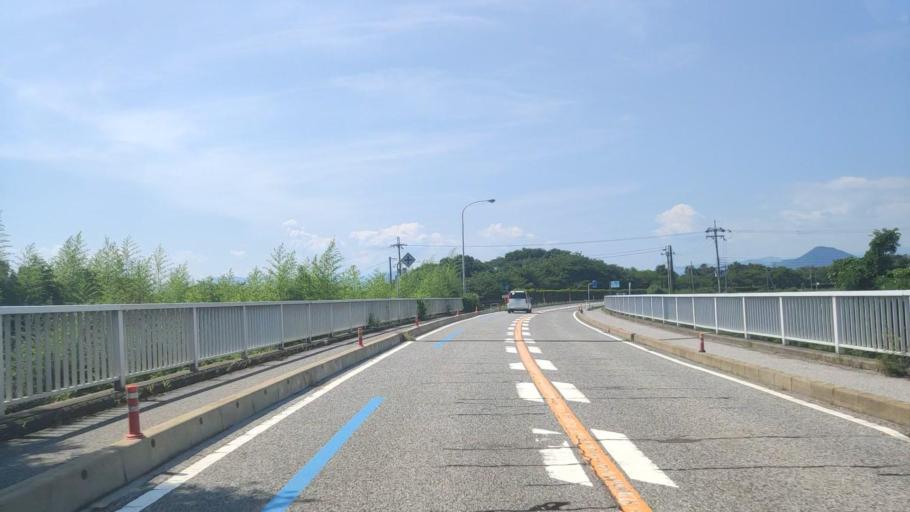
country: JP
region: Shiga Prefecture
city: Nagahama
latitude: 35.3902
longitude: 136.2181
